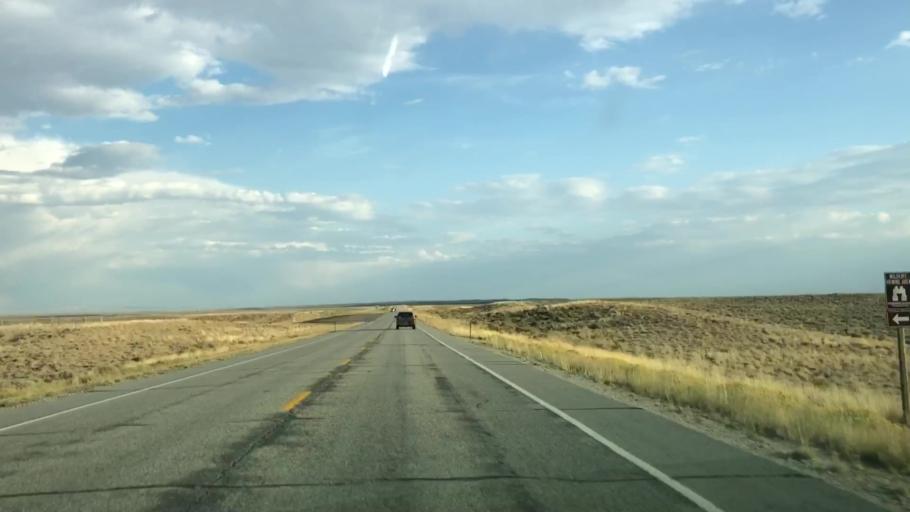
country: US
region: Wyoming
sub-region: Sublette County
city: Marbleton
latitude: 42.3296
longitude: -109.5151
